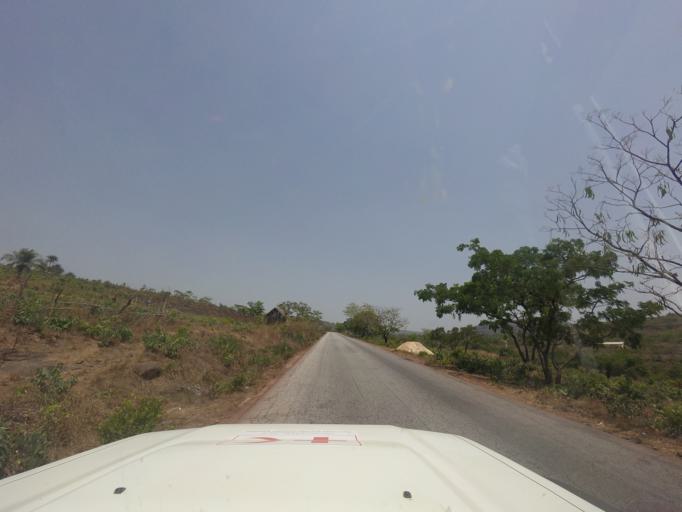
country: GN
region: Kindia
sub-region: Coyah
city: Coyah
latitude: 9.8286
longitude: -13.1182
